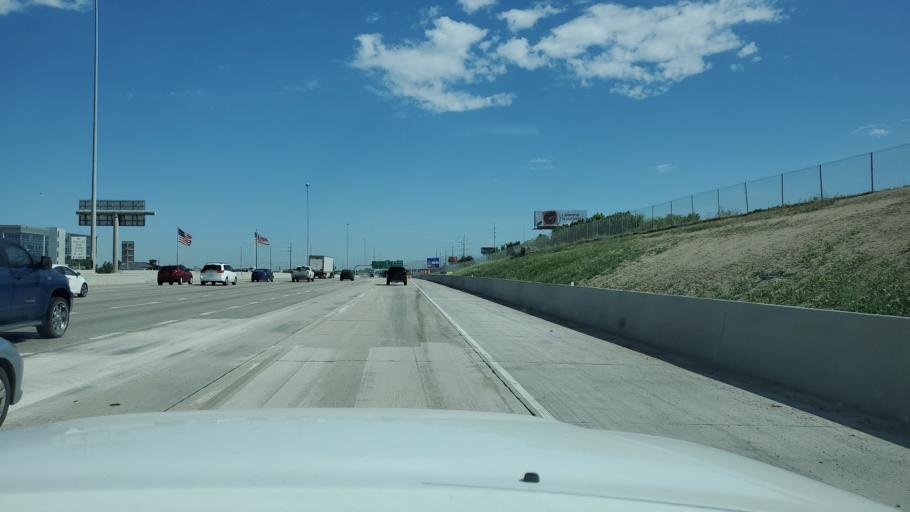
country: US
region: Utah
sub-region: Salt Lake County
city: Sandy City
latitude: 40.5758
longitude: -111.8989
